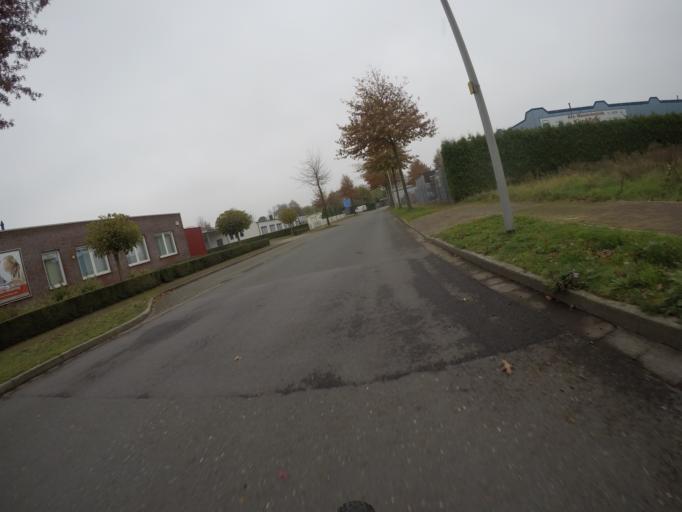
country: DE
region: North Rhine-Westphalia
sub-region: Regierungsbezirk Dusseldorf
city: Bocholt
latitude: 51.8162
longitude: 6.5785
